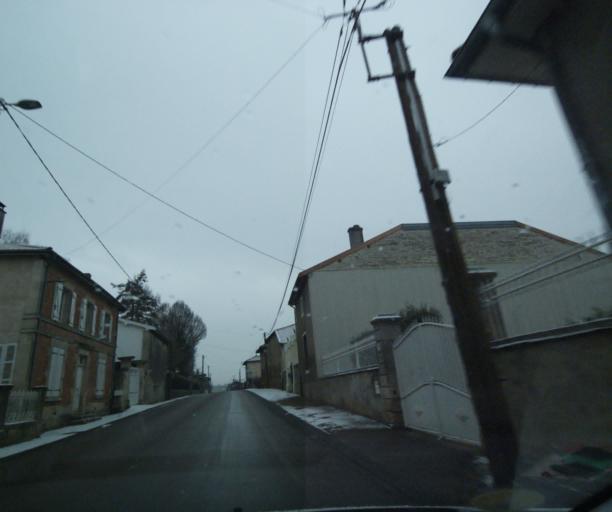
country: FR
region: Champagne-Ardenne
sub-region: Departement de la Haute-Marne
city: Wassy
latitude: 48.4566
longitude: 4.9636
